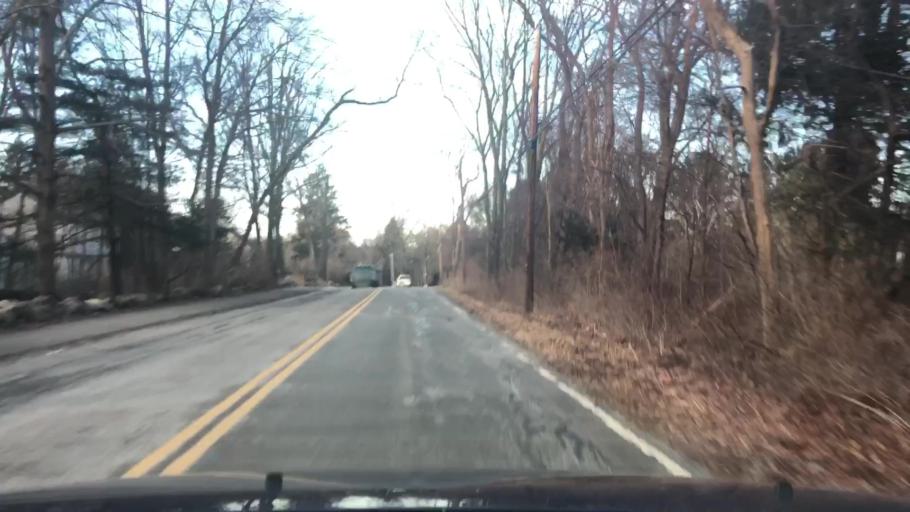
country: US
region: Massachusetts
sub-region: Essex County
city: Andover
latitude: 42.6760
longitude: -71.1148
